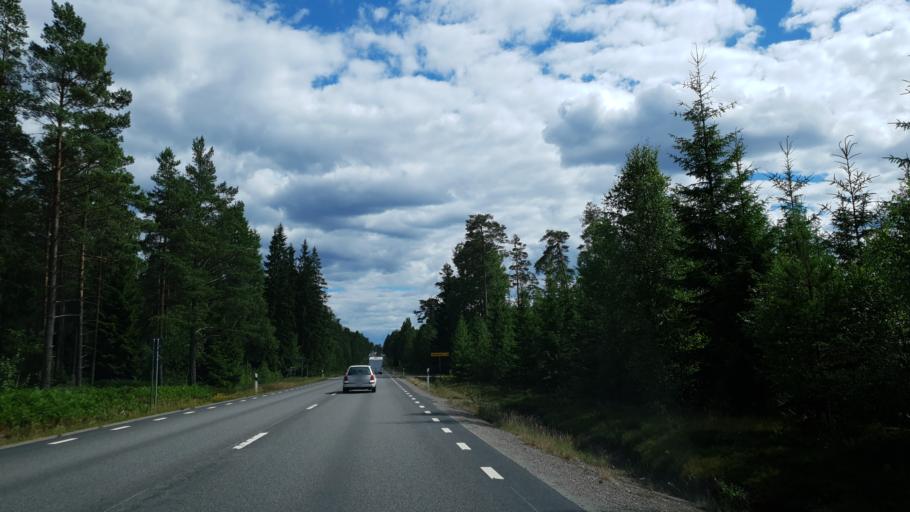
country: SE
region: Kronoberg
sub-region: Lessebo Kommun
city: Lessebo
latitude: 56.8254
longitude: 15.4035
